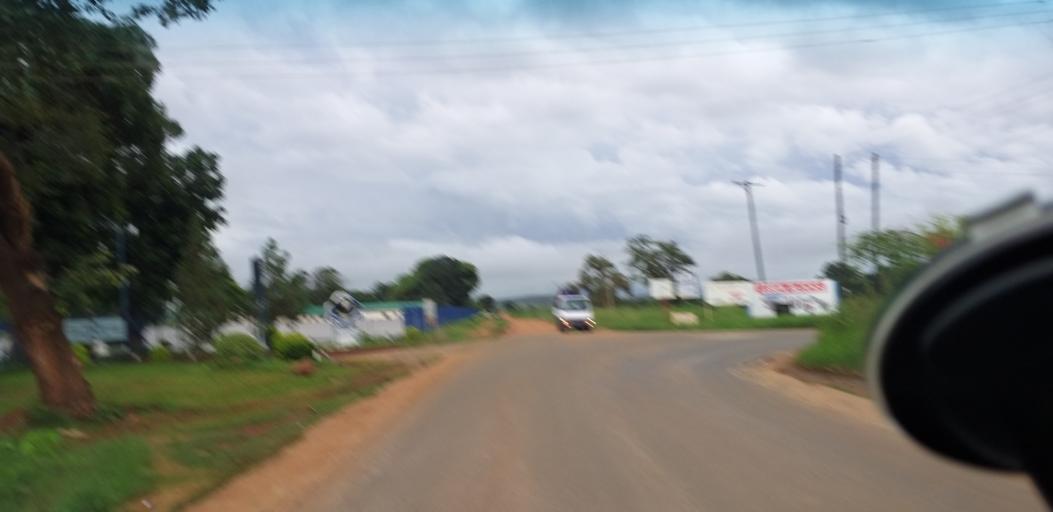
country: ZM
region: Lusaka
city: Lusaka
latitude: -15.5204
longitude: 28.2975
